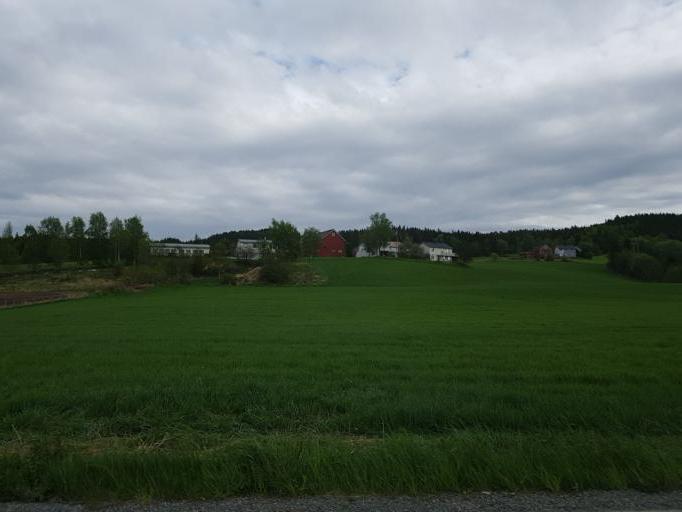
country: NO
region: Nord-Trondelag
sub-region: Levanger
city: Skogn
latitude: 63.7104
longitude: 11.2490
